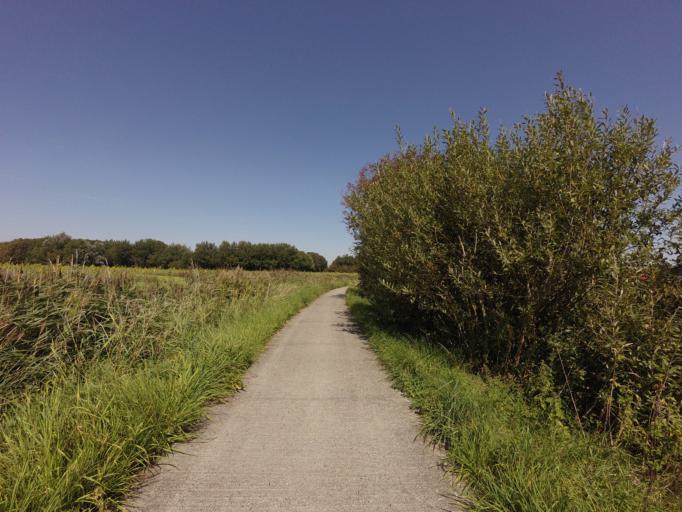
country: NL
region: Friesland
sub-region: Gemeente Dongeradeel
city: Anjum
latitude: 53.4000
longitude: 6.0803
